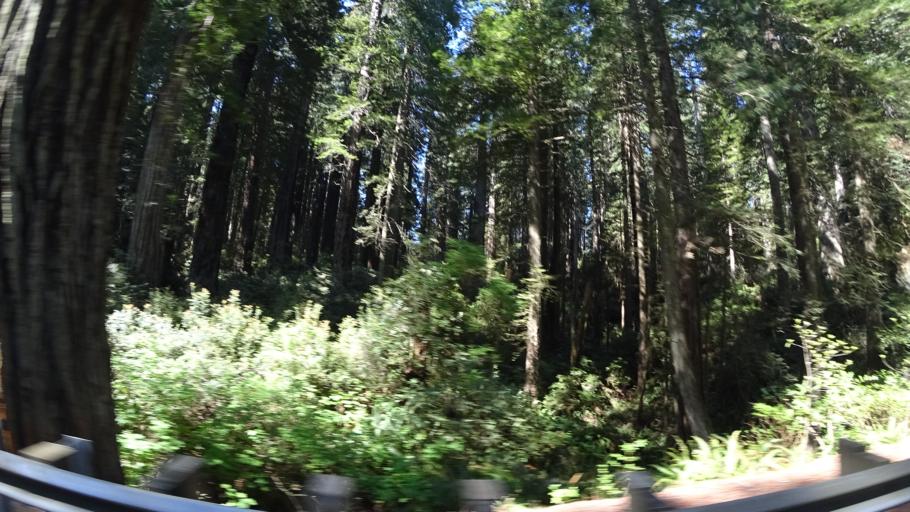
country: US
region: California
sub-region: Del Norte County
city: Bertsch-Oceanview
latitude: 41.6494
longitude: -124.1142
